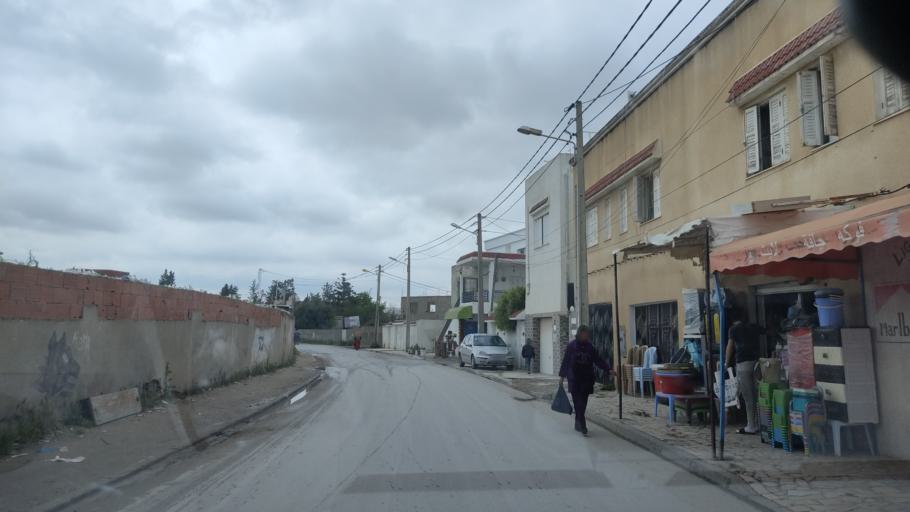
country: TN
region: Ariana
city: Ariana
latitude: 36.8851
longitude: 10.2185
